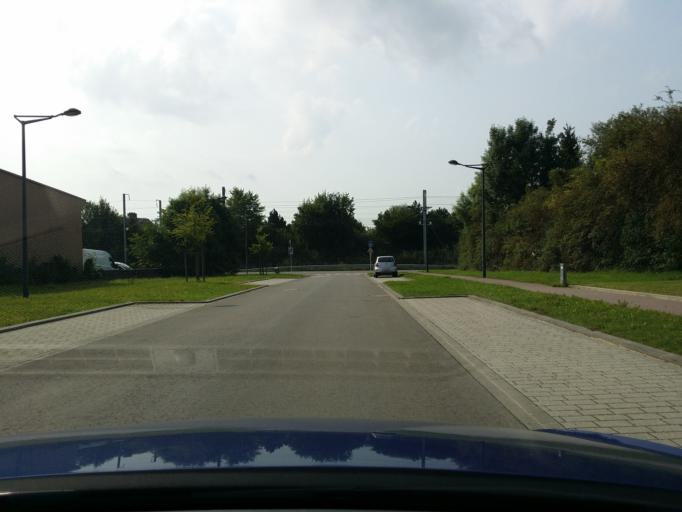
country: LU
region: Luxembourg
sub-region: Canton de Luxembourg
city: Bertrange
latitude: 49.6150
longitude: 6.0529
